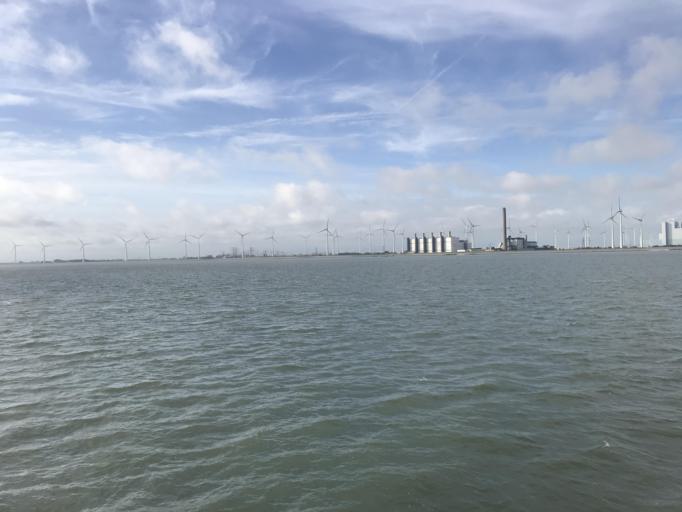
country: NL
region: Groningen
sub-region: Gemeente Delfzijl
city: Delfzijl
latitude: 53.4397
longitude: 6.9047
